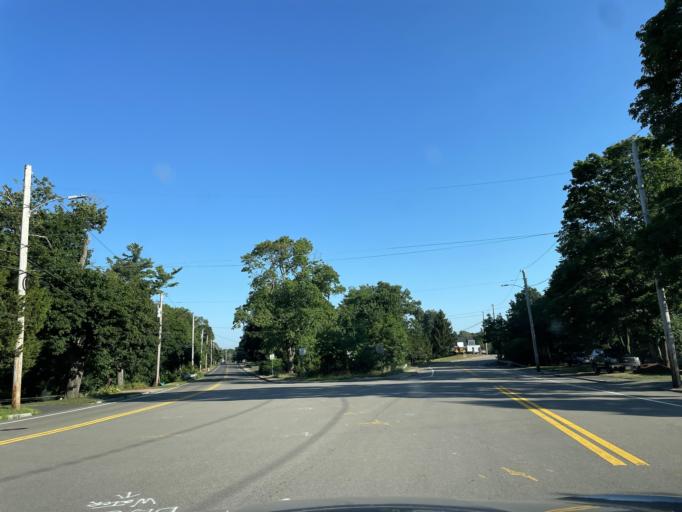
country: US
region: Massachusetts
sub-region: Bristol County
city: Mansfield
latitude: 42.0341
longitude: -71.2307
